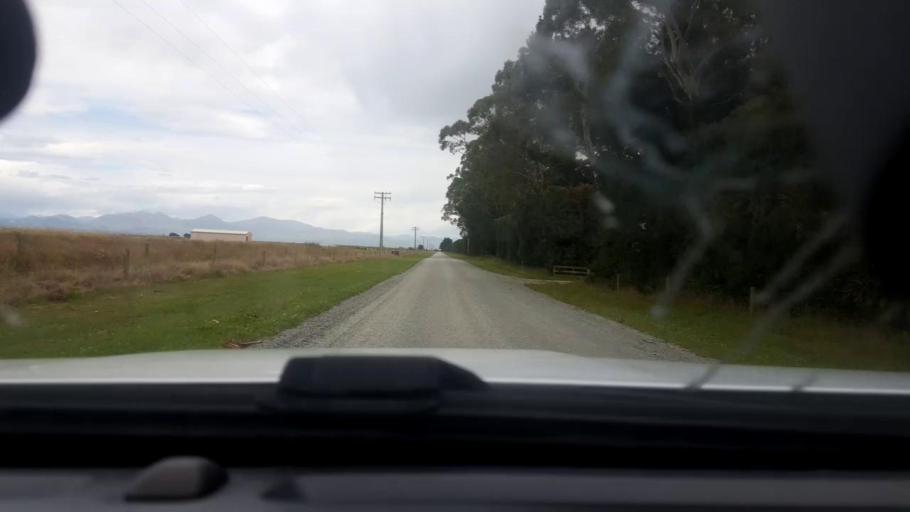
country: NZ
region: Canterbury
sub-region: Timaru District
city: Pleasant Point
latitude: -44.1504
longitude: 171.3940
